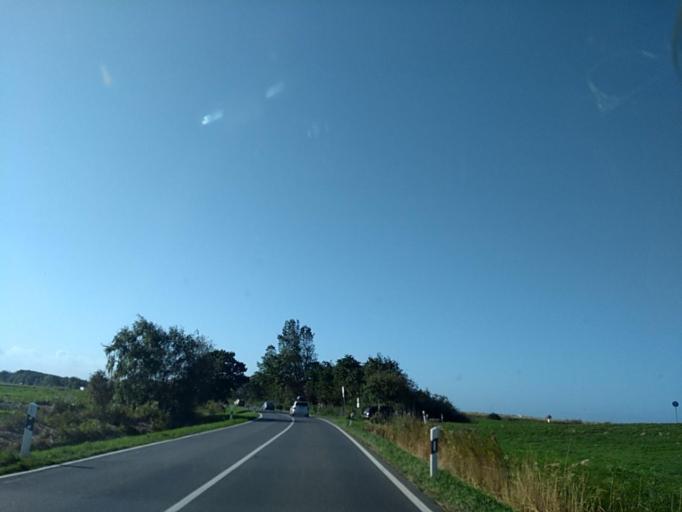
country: DE
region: Mecklenburg-Vorpommern
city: Ostseebad Dierhagen
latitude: 54.3433
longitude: 12.3865
